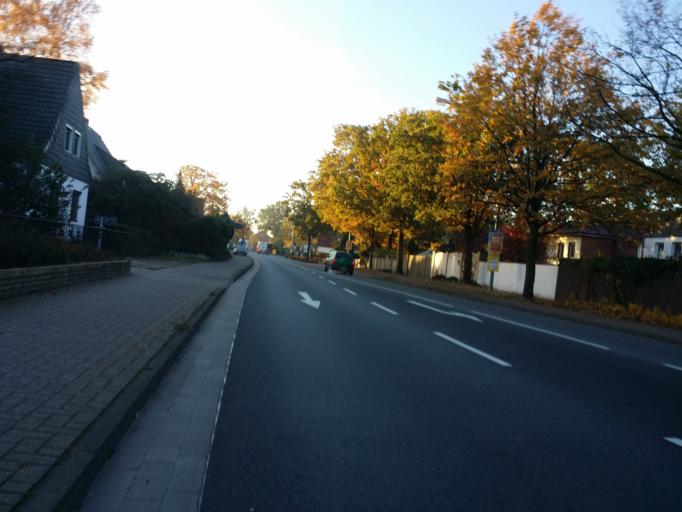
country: DE
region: Lower Saxony
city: Kirchseelte
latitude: 53.0008
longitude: 8.7046
